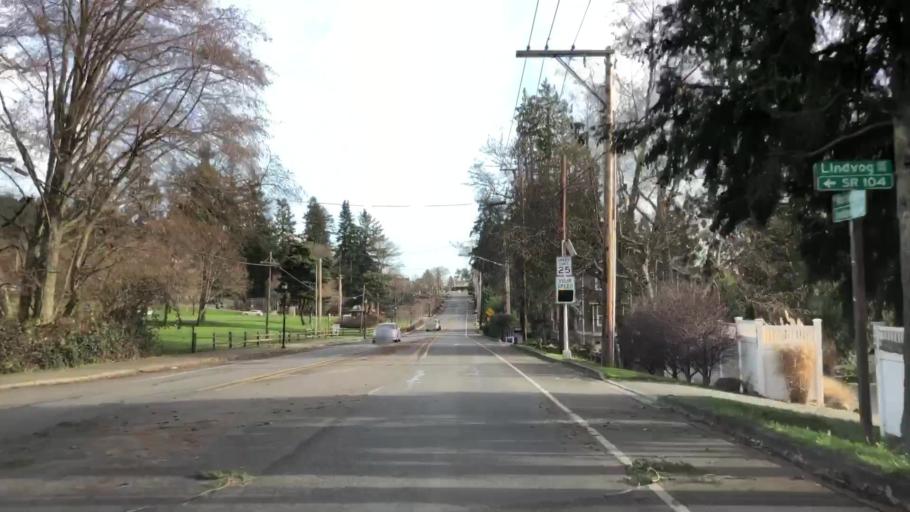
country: US
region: Washington
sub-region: Kitsap County
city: Kingston
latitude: 47.7984
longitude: -122.5047
